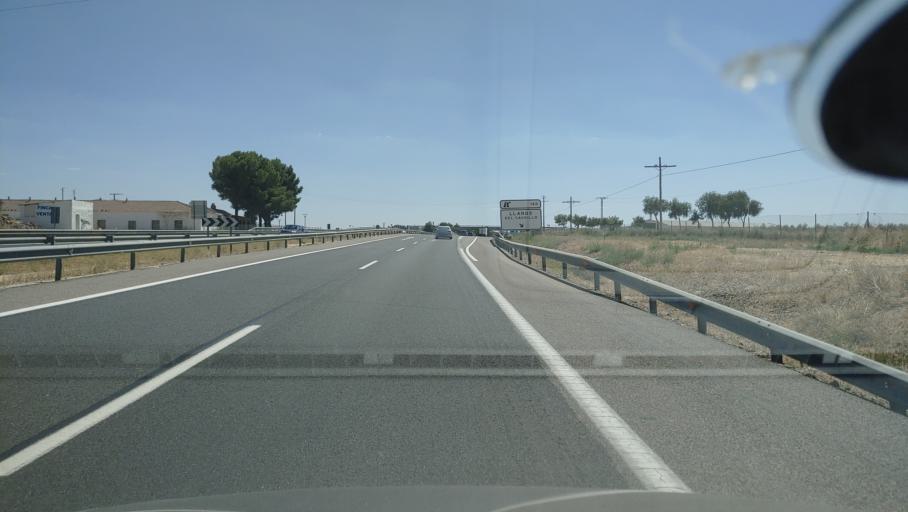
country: ES
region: Castille-La Mancha
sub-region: Provincia de Ciudad Real
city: Villarta de San Juan
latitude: 39.1272
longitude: -3.3783
